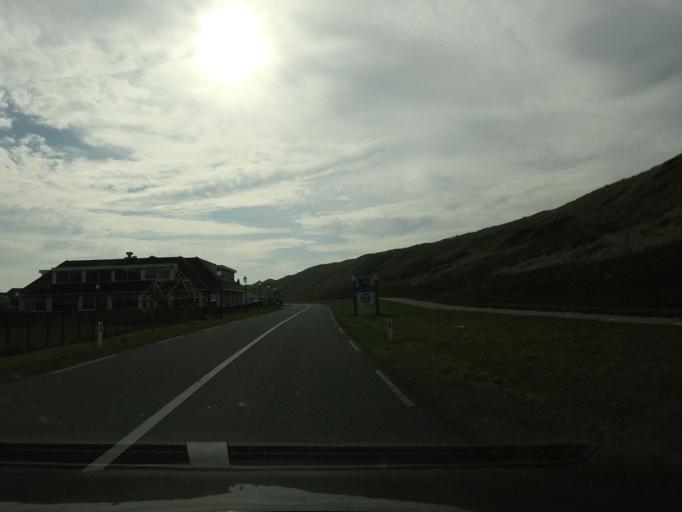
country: NL
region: North Holland
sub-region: Gemeente Schagen
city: Schagen
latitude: 52.8442
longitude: 4.6967
